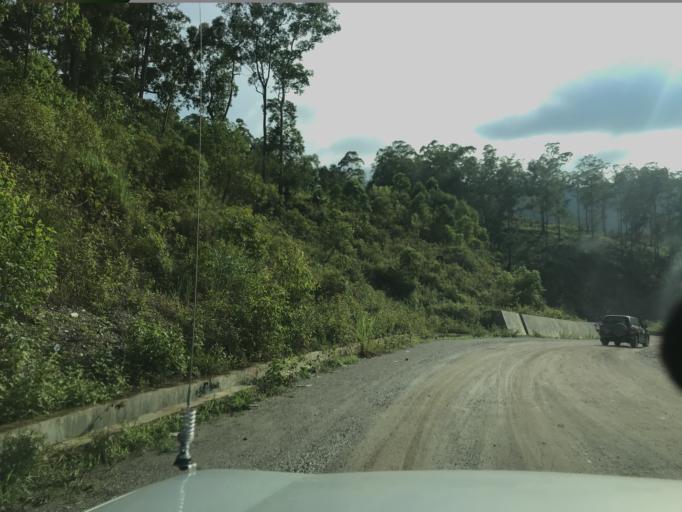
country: TL
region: Aileu
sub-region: Aileu Villa
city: Aileu
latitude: -8.6630
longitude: 125.5439
